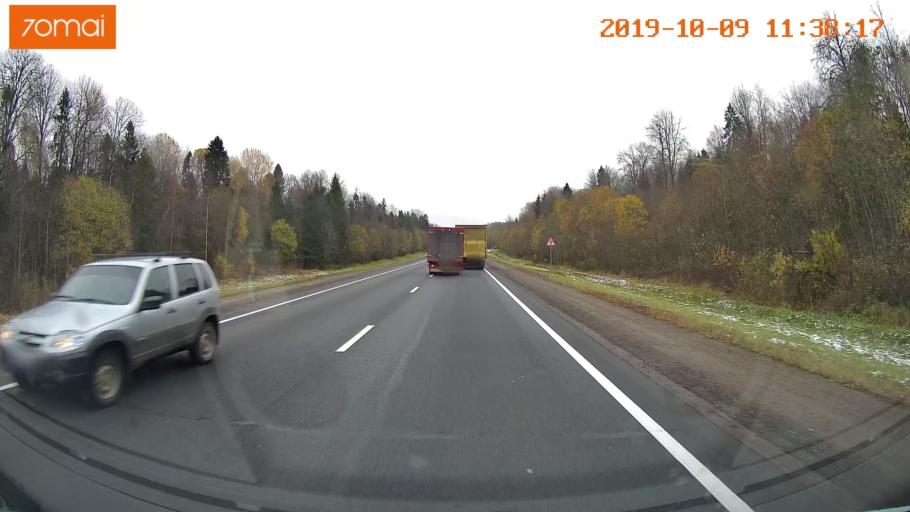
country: RU
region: Vologda
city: Gryazovets
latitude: 58.9698
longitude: 40.1544
